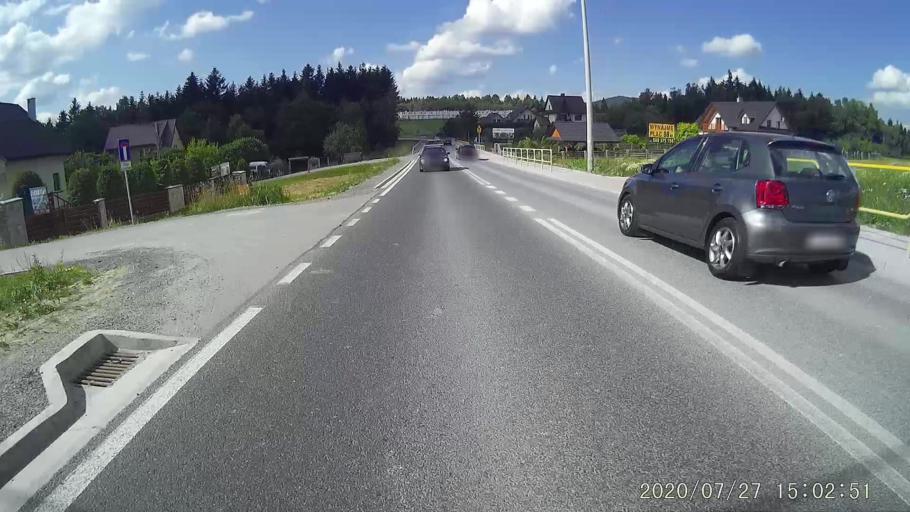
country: PL
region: Lesser Poland Voivodeship
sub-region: Powiat suski
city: Naprawa
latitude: 49.6701
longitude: 19.8915
